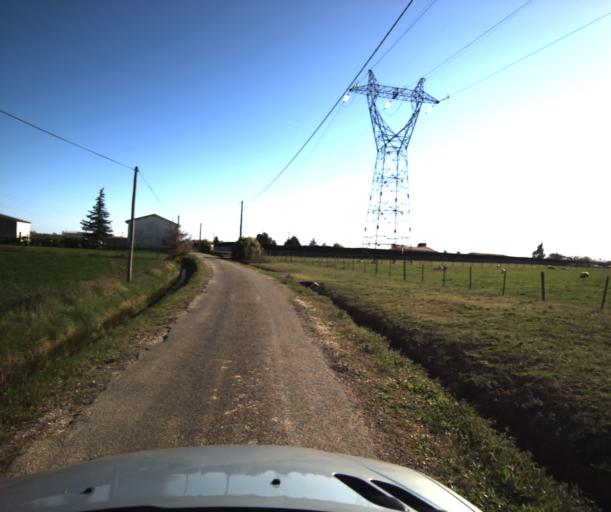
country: FR
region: Midi-Pyrenees
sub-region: Departement du Tarn-et-Garonne
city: Bressols
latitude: 43.9449
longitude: 1.3287
